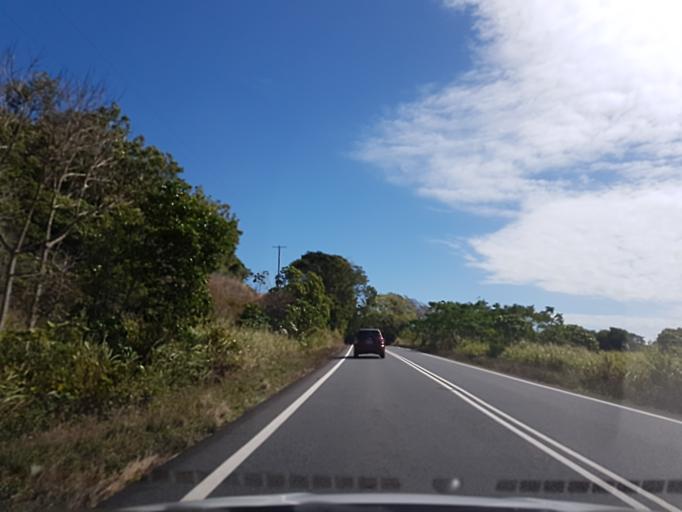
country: AU
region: Queensland
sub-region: Cairns
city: Port Douglas
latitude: -16.5658
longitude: 145.5017
